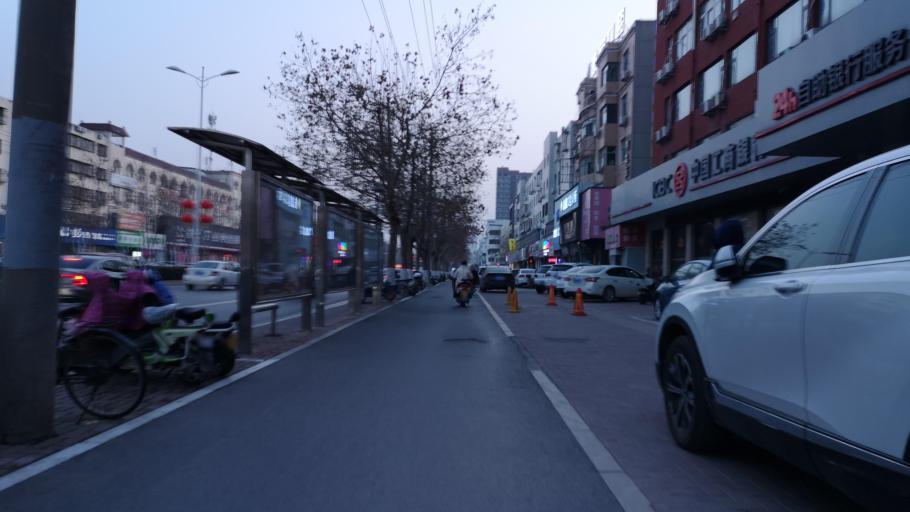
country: CN
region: Henan Sheng
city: Zhongyuanlu
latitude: 35.7673
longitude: 115.0686
